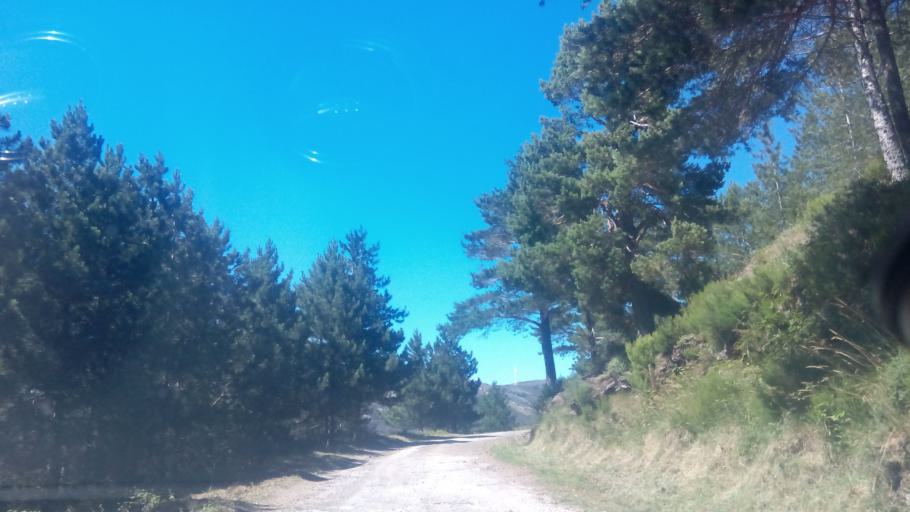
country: PT
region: Vila Real
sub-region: Mesao Frio
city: Mesao Frio
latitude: 41.2727
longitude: -7.9218
